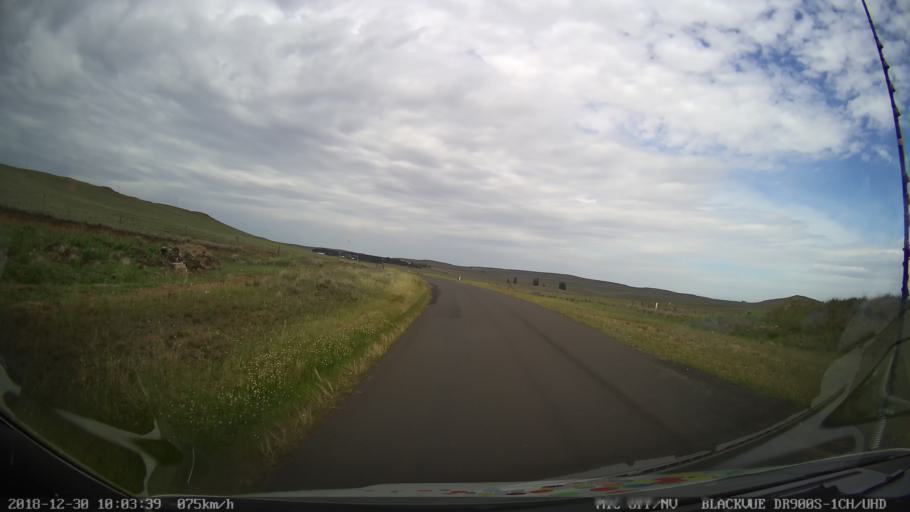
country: AU
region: New South Wales
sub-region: Cooma-Monaro
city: Cooma
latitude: -36.5155
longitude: 149.1544
